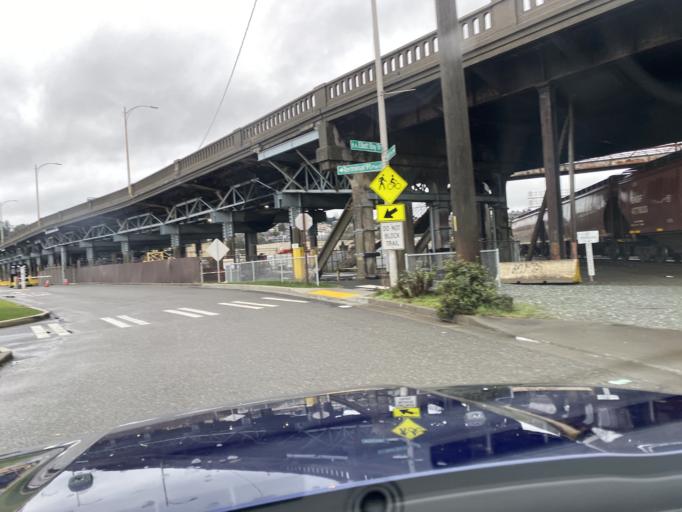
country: US
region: Washington
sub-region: King County
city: Seattle
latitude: 47.6332
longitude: -122.3787
